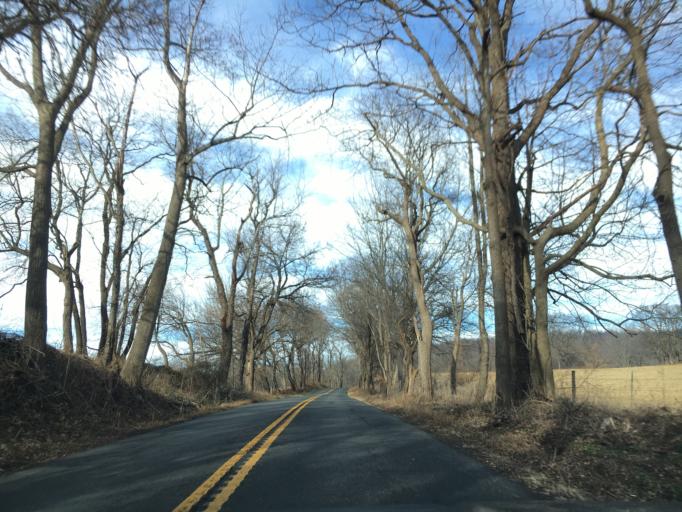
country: US
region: Virginia
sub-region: Warren County
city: Apple Mountain Lake
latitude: 38.8650
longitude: -77.9942
